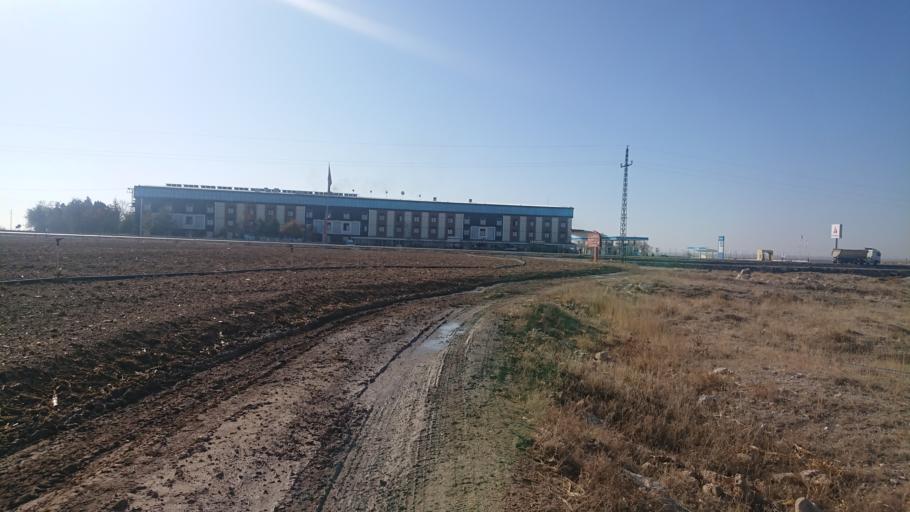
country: TR
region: Aksaray
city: Sultanhani
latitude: 38.2532
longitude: 33.5080
